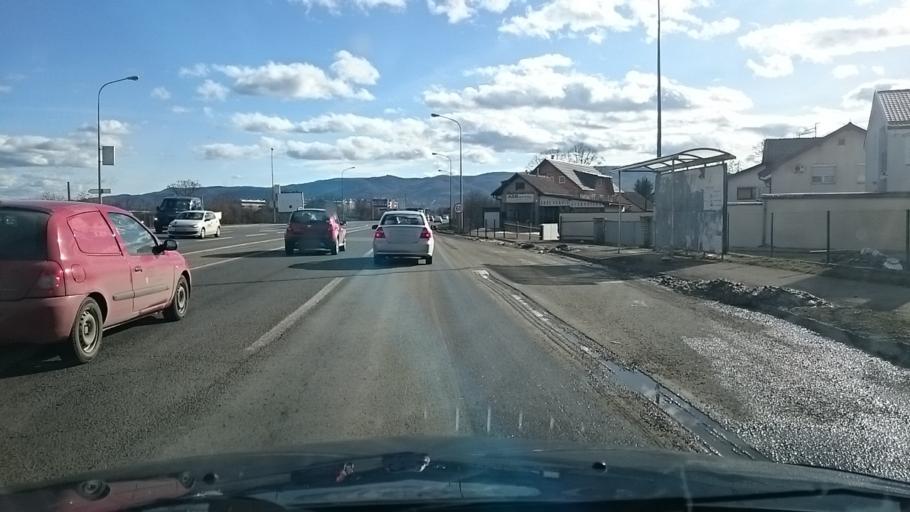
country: BA
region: Republika Srpska
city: Banja Luka
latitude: 44.7963
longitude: 17.1988
